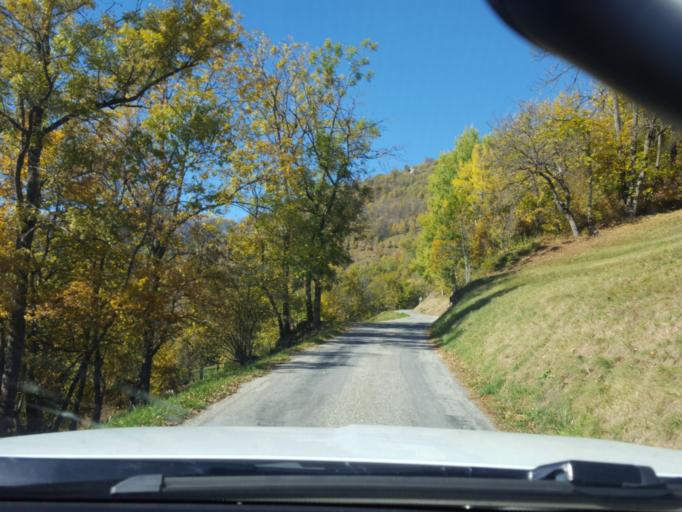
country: FR
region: Rhone-Alpes
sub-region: Departement de la Savoie
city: Bourg-Saint-Maurice
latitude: 45.6292
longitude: 6.7723
